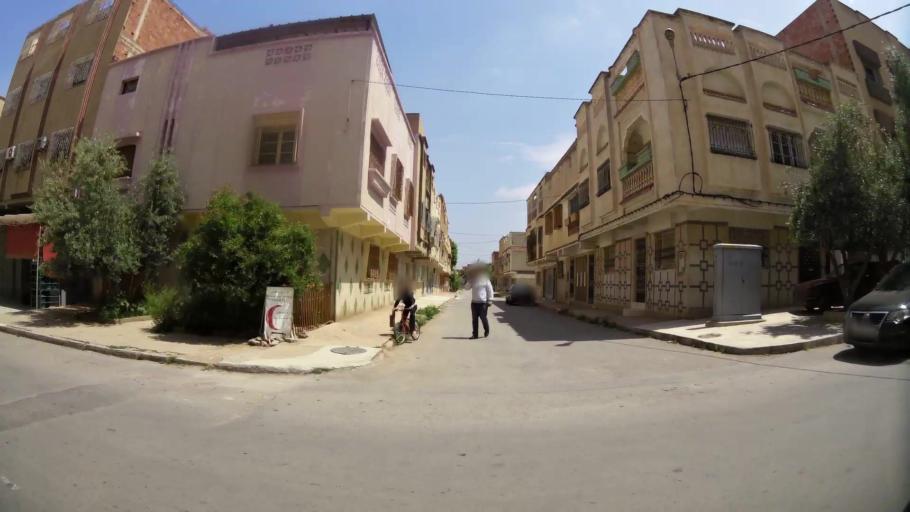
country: MA
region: Oriental
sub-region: Oujda-Angad
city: Oujda
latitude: 34.6883
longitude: -1.8844
